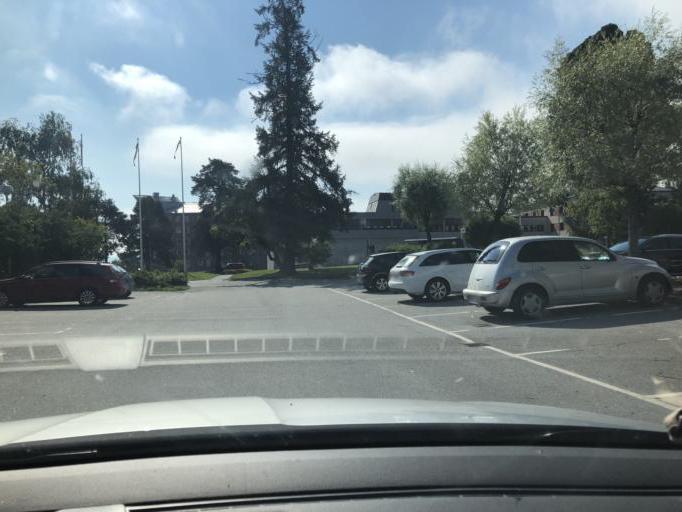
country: SE
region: Vaesternorrland
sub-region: OErnskoeldsviks Kommun
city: Ornskoldsvik
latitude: 63.2996
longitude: 18.7145
